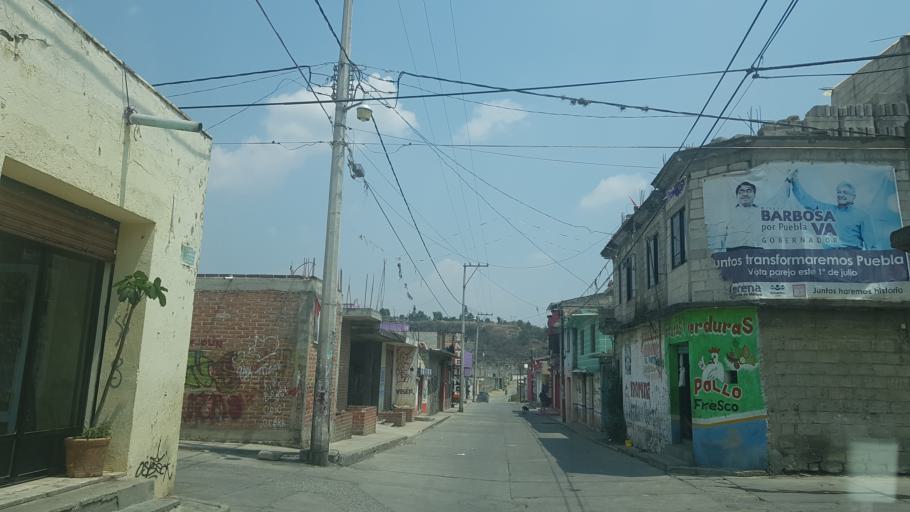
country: MX
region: Puebla
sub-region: San Nicolas de los Ranchos
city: San Pedro Yancuitlalpan
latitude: 19.0761
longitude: -98.4844
